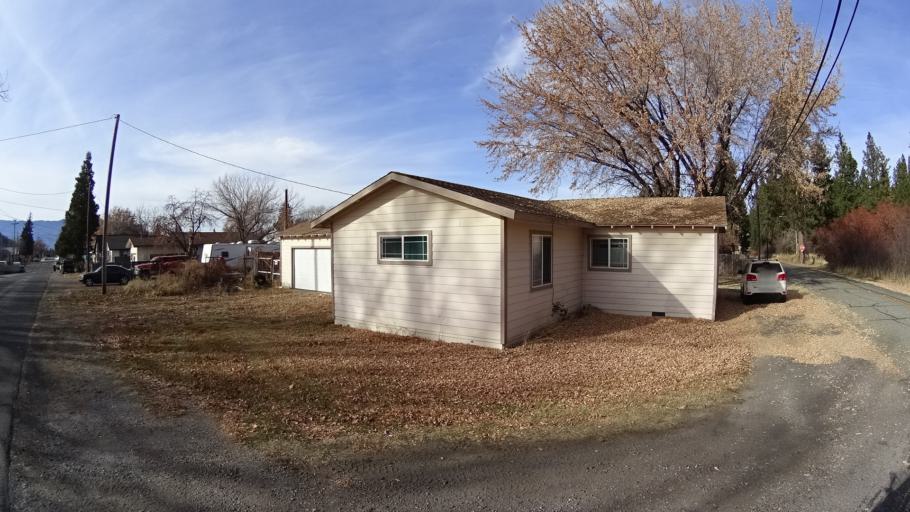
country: US
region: California
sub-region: Siskiyou County
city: Weed
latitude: 41.4386
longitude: -122.3767
